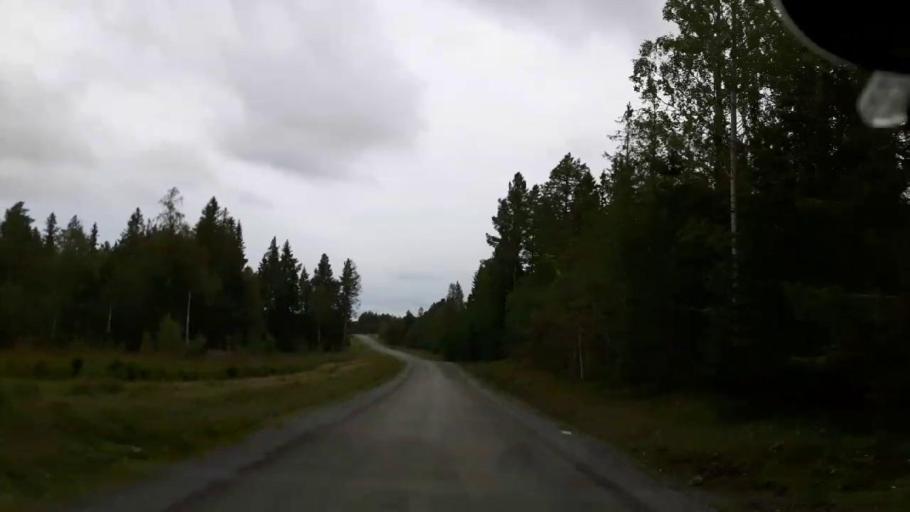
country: SE
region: Jaemtland
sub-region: OEstersunds Kommun
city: Ostersund
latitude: 63.1042
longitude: 14.5465
